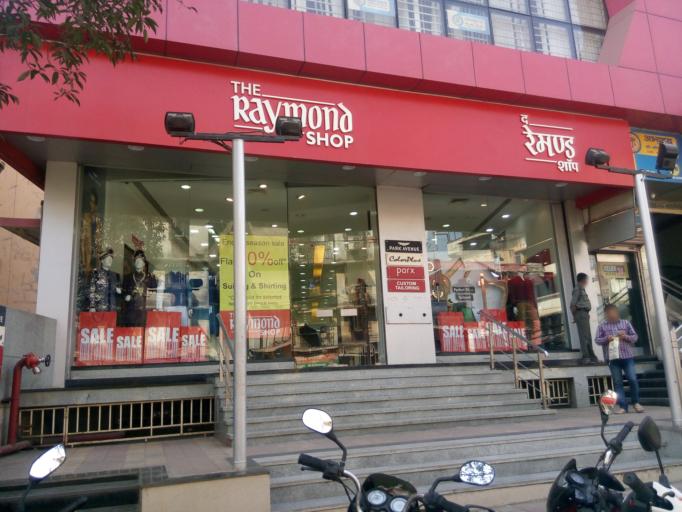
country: IN
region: Maharashtra
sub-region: Thane
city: Dombivli
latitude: 19.2098
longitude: 73.0938
